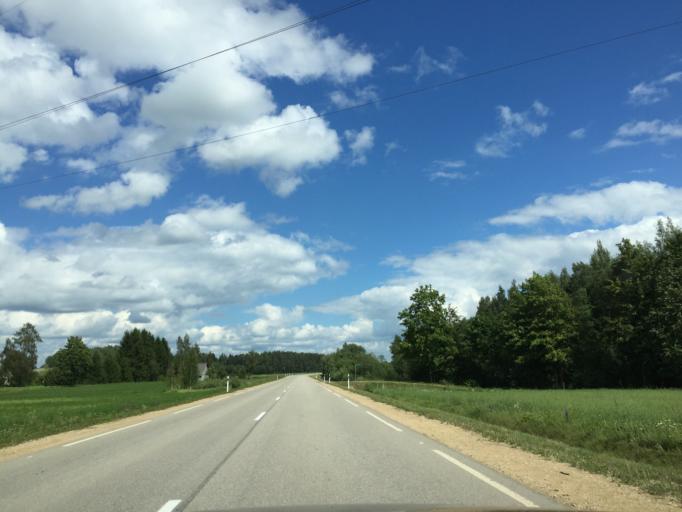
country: LV
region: Malpils
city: Malpils
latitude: 56.8984
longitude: 24.9082
